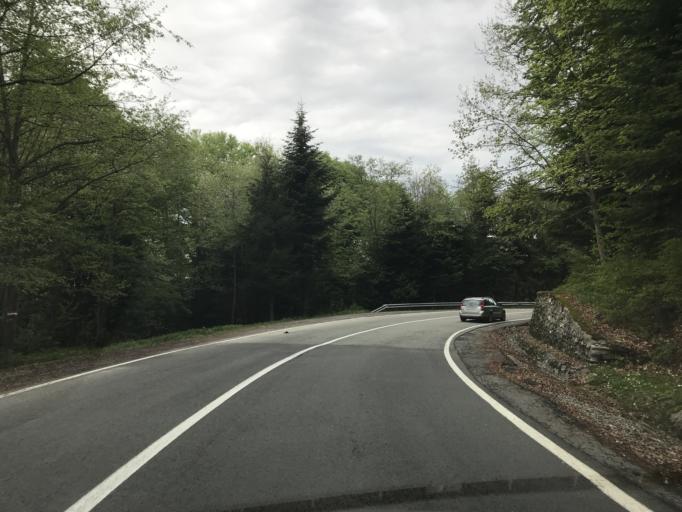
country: RO
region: Sibiu
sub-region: Comuna Cartisoara
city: Cartisoara
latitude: 45.6658
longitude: 24.5886
